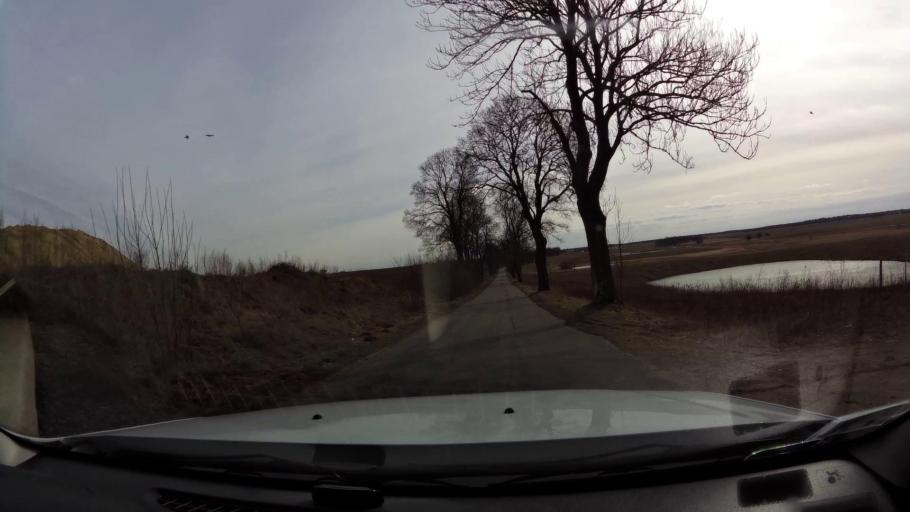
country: PL
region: West Pomeranian Voivodeship
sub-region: Powiat stargardzki
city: Insko
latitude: 53.4664
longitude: 15.5992
